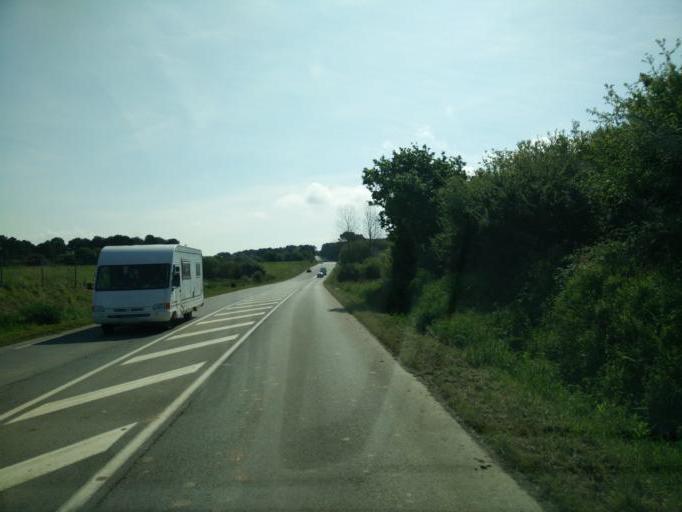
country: FR
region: Brittany
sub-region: Departement du Finistere
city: Crozon
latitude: 48.2486
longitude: -4.4540
